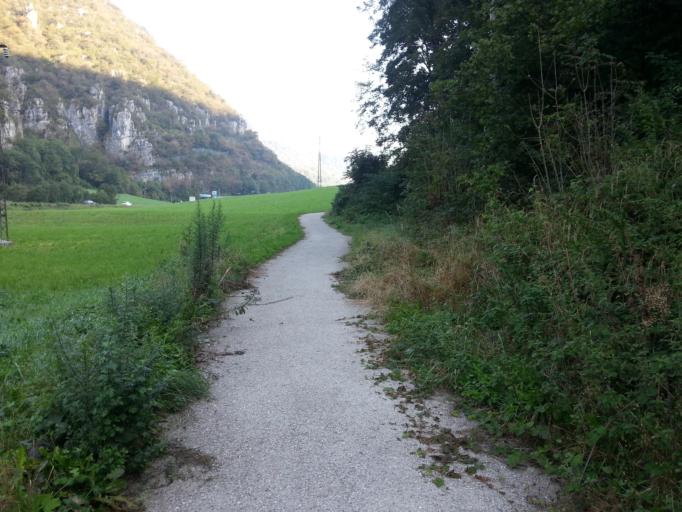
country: IT
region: Lombardy
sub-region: Provincia di Lecco
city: Ballabio
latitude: 45.9122
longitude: 9.4333
